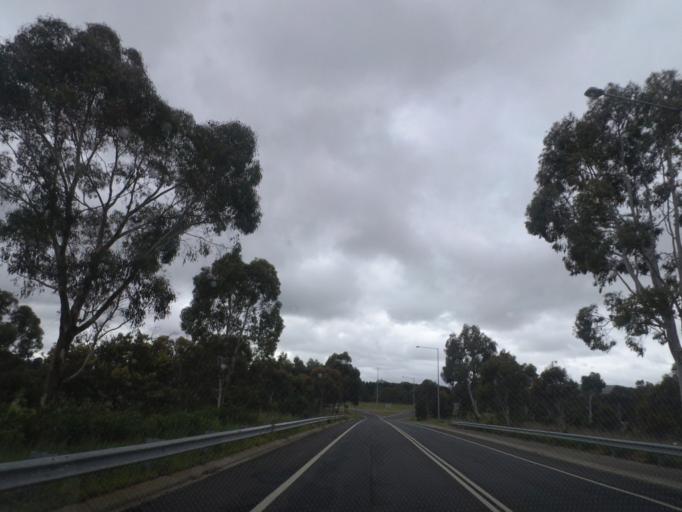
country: AU
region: Victoria
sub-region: Hume
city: Sunbury
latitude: -37.3198
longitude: 144.5266
